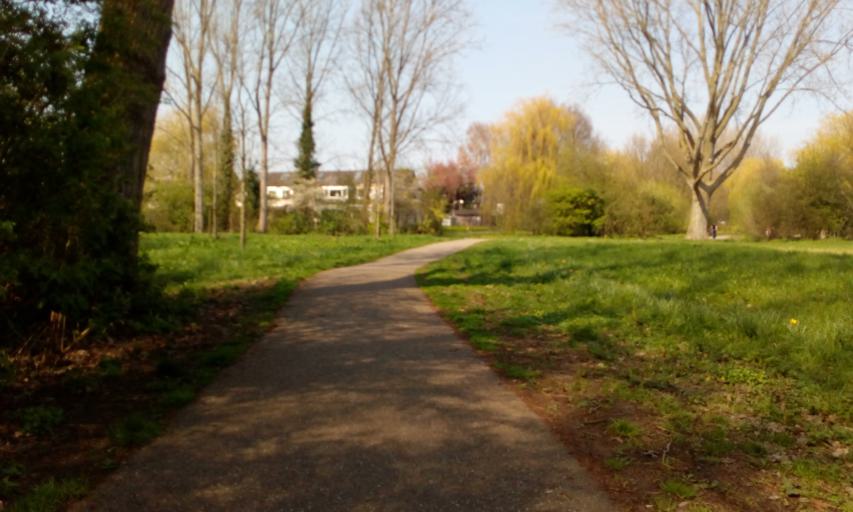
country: NL
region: South Holland
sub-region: Gemeente Spijkenisse
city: Spijkenisse
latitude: 51.8307
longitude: 4.3505
